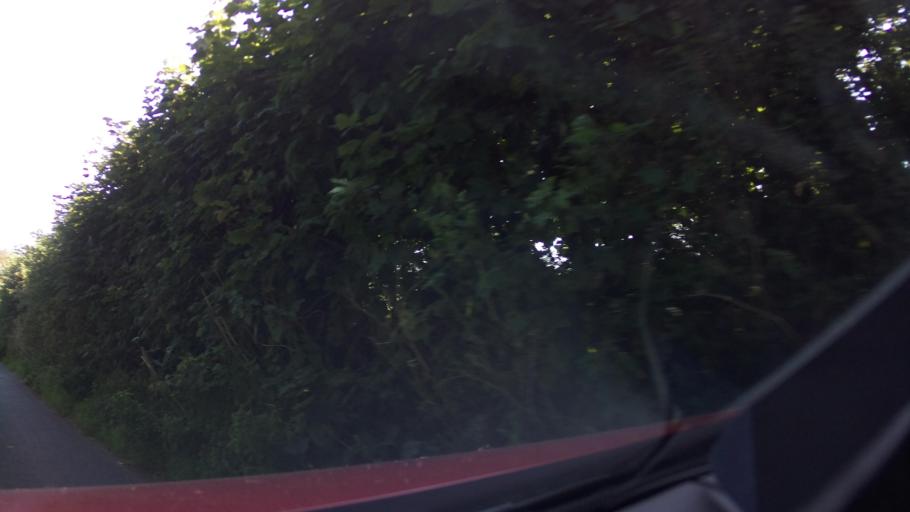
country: GB
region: England
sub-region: Devon
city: Totnes
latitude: 50.4036
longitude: -3.7125
